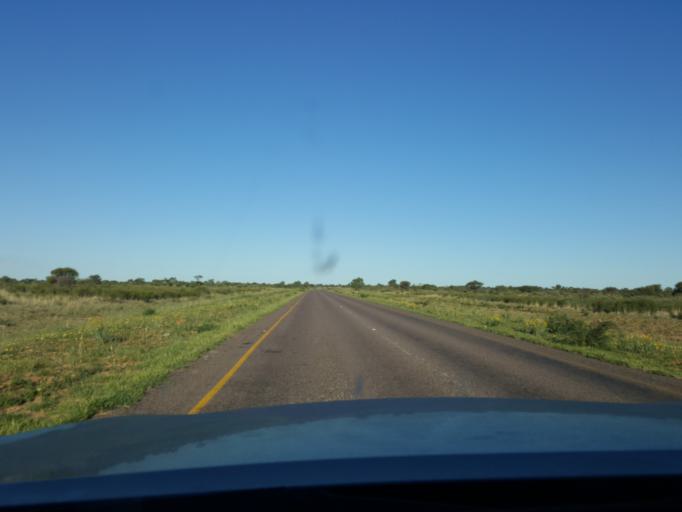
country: BW
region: Southern
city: Khakhea
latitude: -24.3015
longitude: 23.3919
